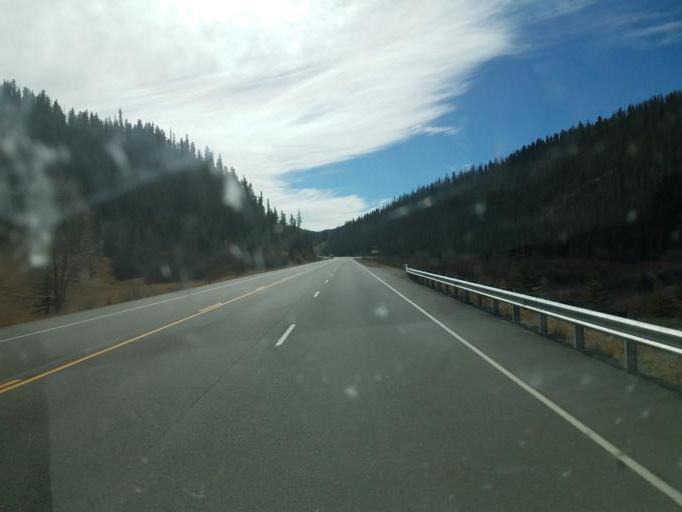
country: US
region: Colorado
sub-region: Mineral County
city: Creede
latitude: 37.5341
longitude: -106.7710
